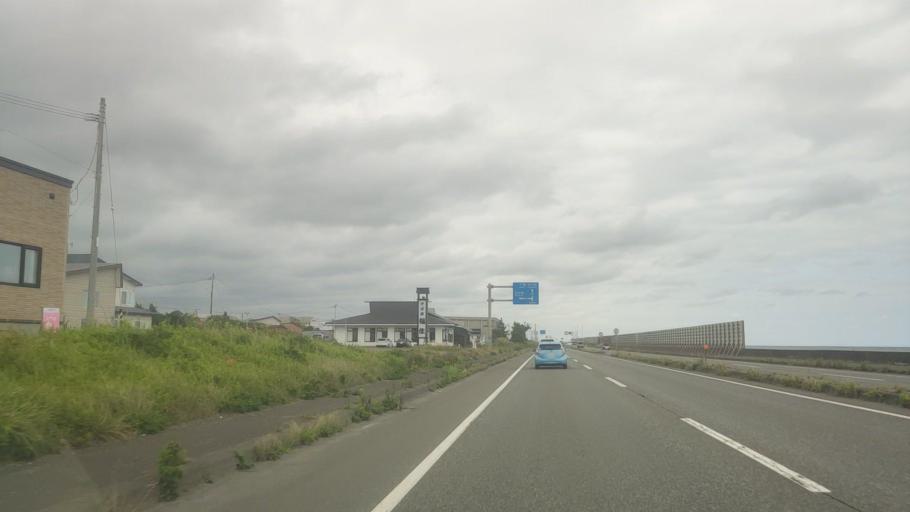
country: JP
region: Hokkaido
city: Shiraoi
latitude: 42.5480
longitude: 141.3609
